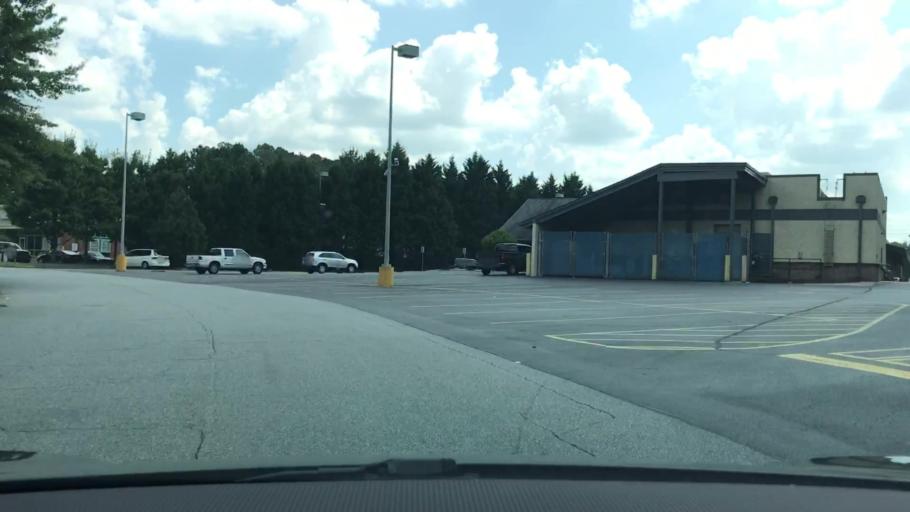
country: US
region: Georgia
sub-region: Gwinnett County
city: Buford
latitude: 34.0877
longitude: -83.9915
